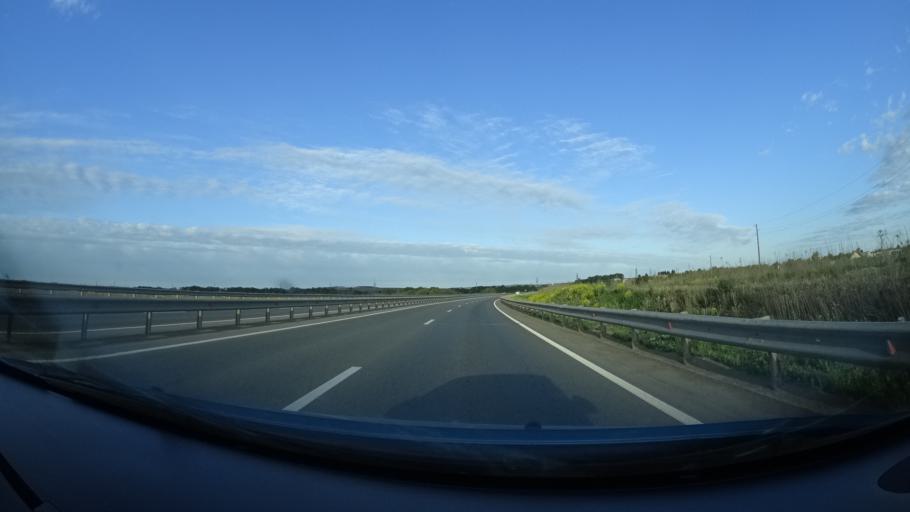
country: RU
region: Perm
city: Kultayevo
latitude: 57.8881
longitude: 55.9416
